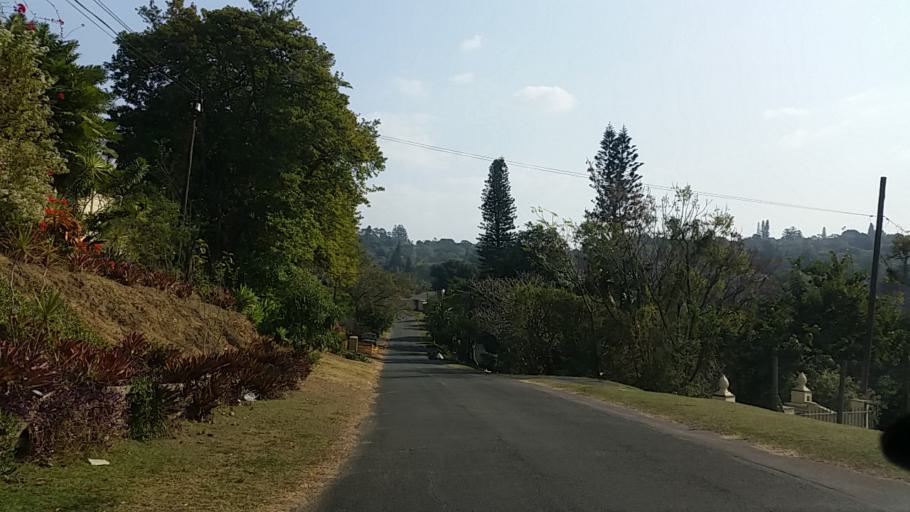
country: ZA
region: KwaZulu-Natal
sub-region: eThekwini Metropolitan Municipality
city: Berea
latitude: -29.8370
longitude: 30.9449
